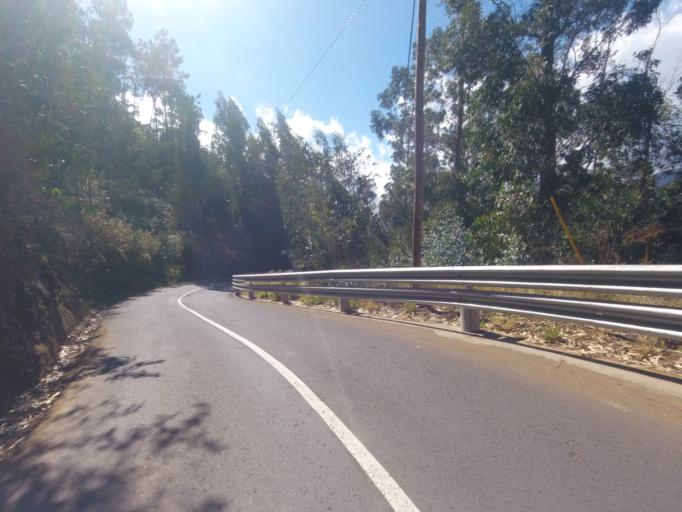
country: PT
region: Madeira
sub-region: Ribeira Brava
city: Campanario
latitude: 32.6876
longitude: -17.0340
